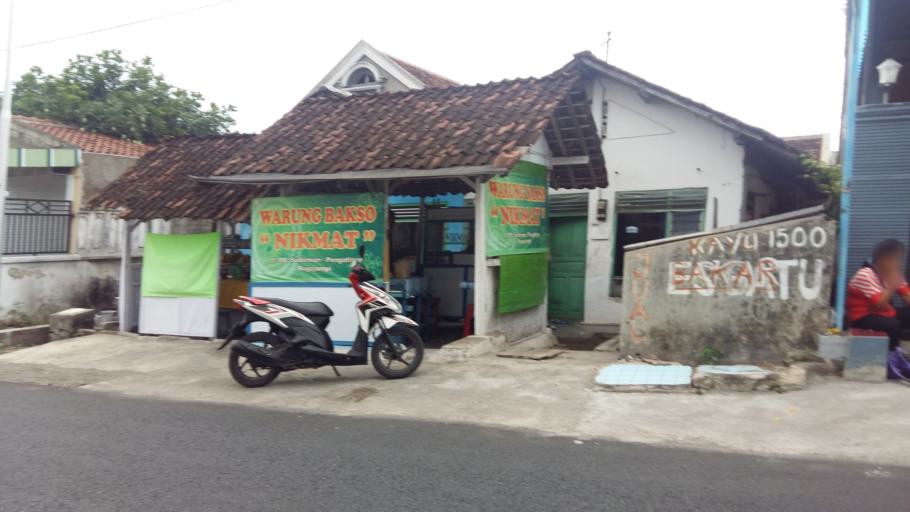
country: ID
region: East Java
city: Krajan
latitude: -8.3065
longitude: 114.2858
